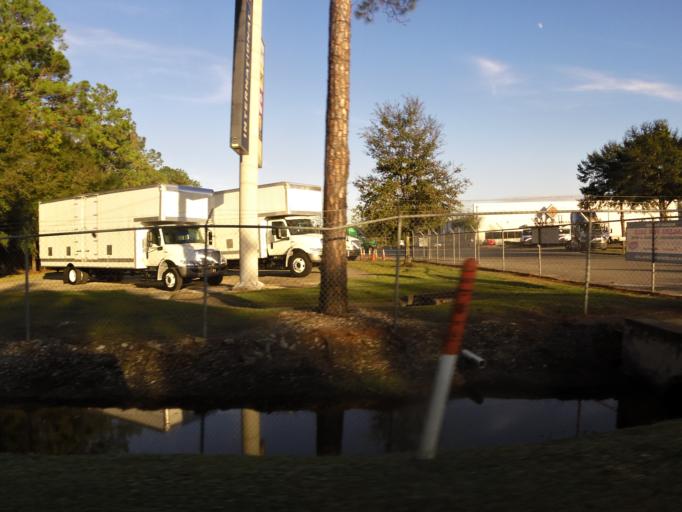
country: US
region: Florida
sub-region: Duval County
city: Jacksonville
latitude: 30.3460
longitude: -81.7646
